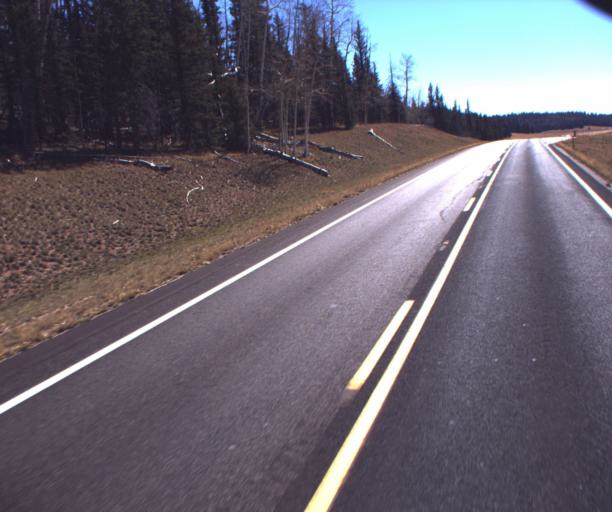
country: US
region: Arizona
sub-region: Coconino County
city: Grand Canyon
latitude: 36.4358
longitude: -112.1340
